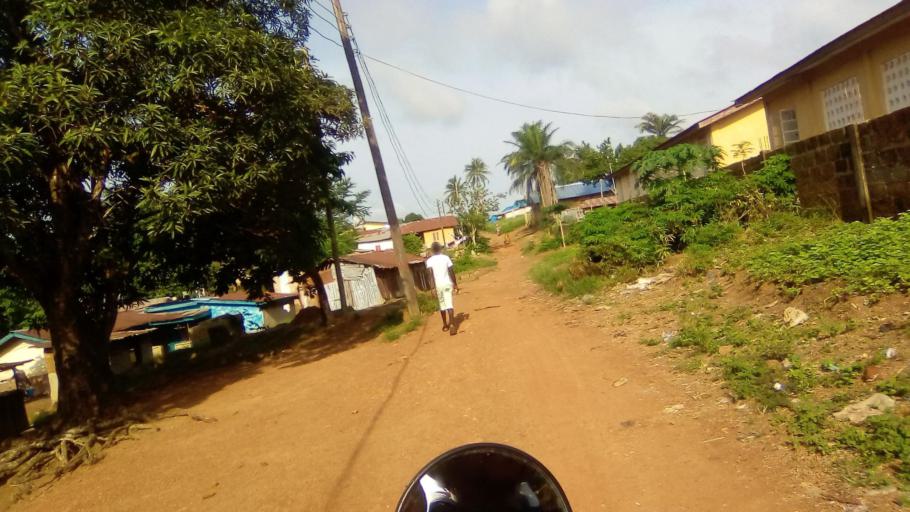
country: SL
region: Southern Province
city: Bo
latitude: 7.9556
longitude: -11.7556
